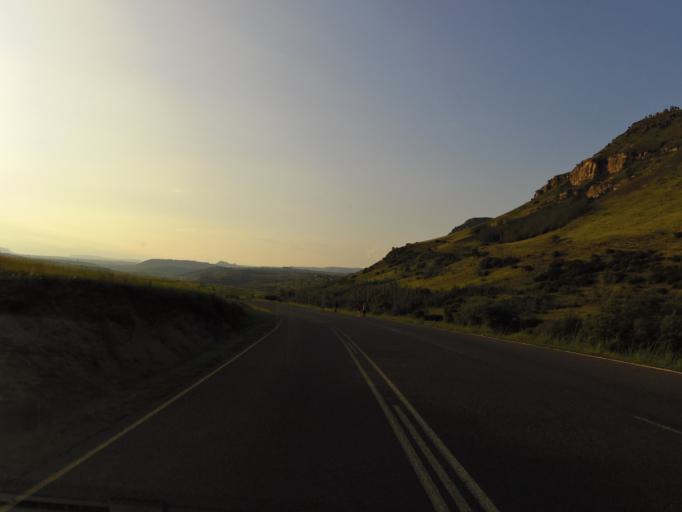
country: LS
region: Leribe
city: Leribe
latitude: -28.9833
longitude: 28.1825
